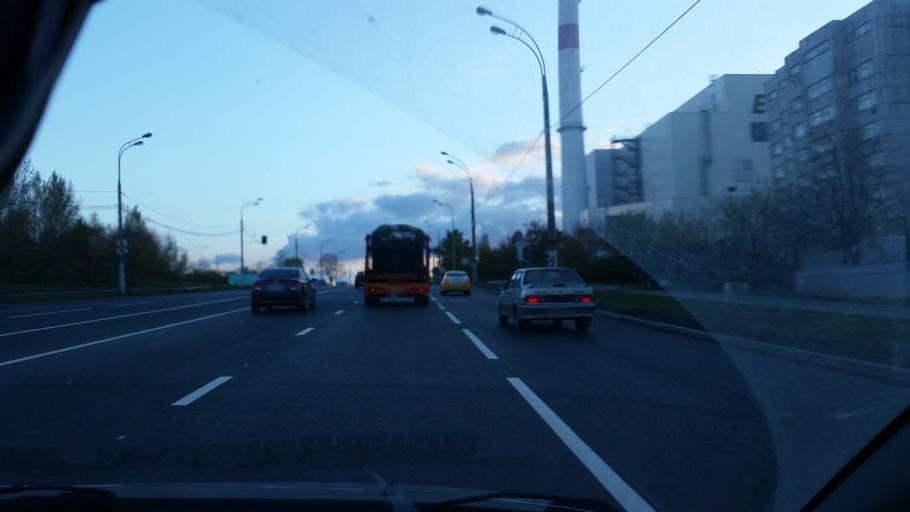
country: RU
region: Moskovskaya
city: Biryulevo Zapadnoye
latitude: 55.6014
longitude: 37.6368
